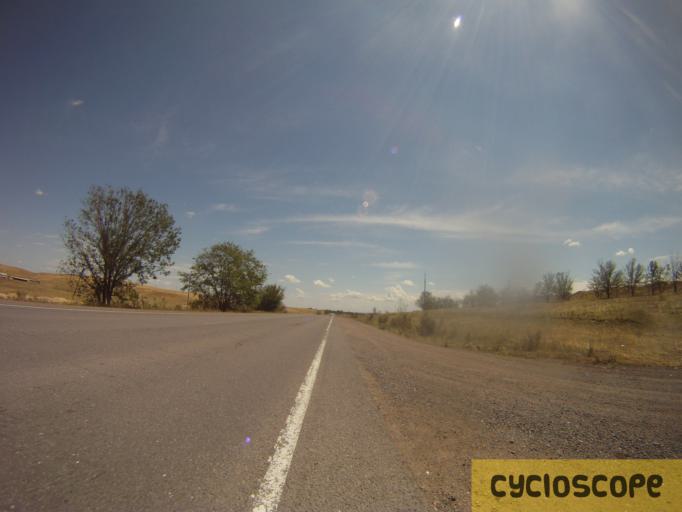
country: KG
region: Chuy
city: Bystrovka
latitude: 43.3214
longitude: 75.9855
